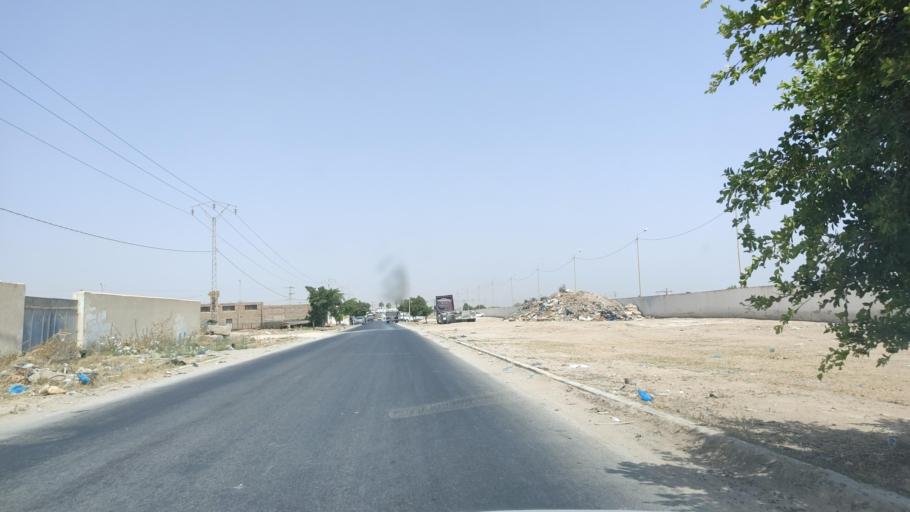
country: TN
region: Safaqis
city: Sfax
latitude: 34.6969
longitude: 10.7215
